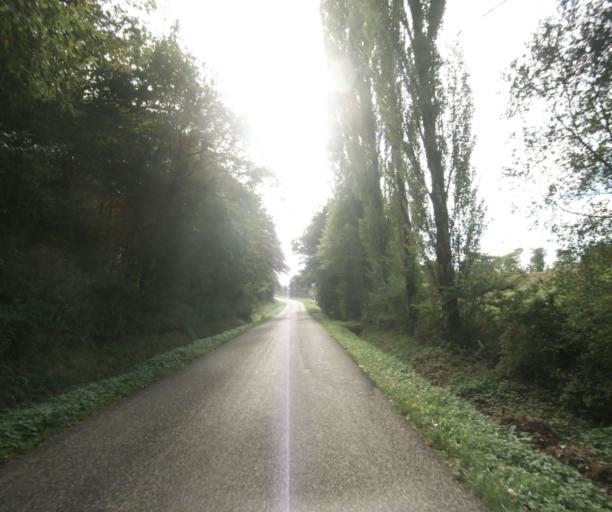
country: FR
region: Midi-Pyrenees
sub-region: Departement du Gers
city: Eauze
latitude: 43.8956
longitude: 0.0963
